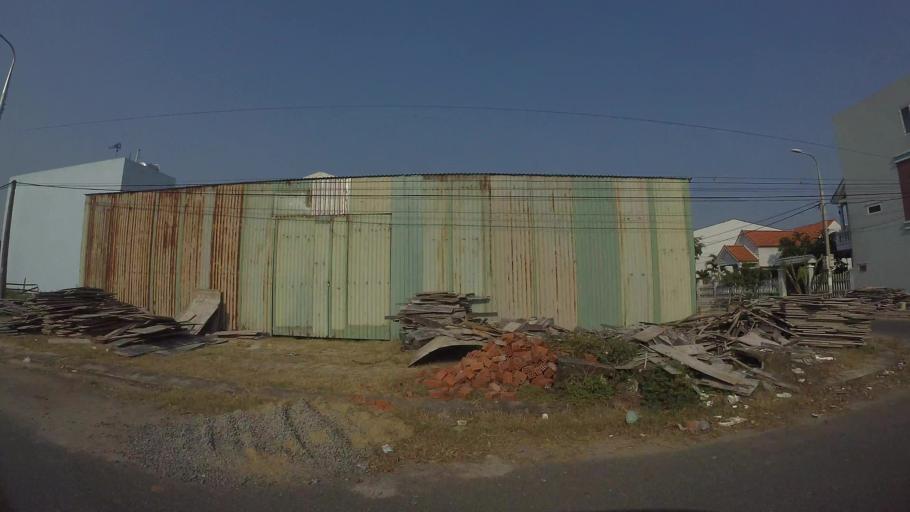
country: VN
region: Da Nang
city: Ngu Hanh Son
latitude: 15.9543
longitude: 108.2556
